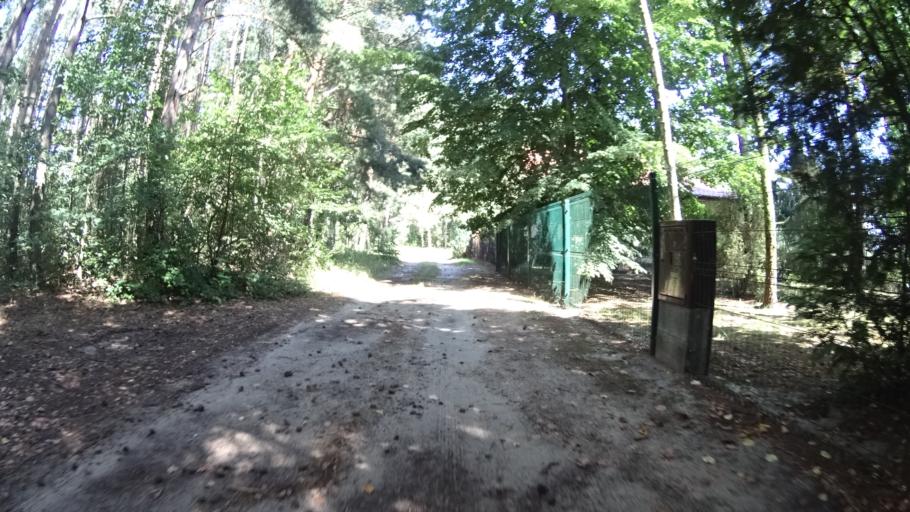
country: PL
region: Masovian Voivodeship
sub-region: Powiat bialobrzeski
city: Bialobrzegi
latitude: 51.6684
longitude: 20.9239
